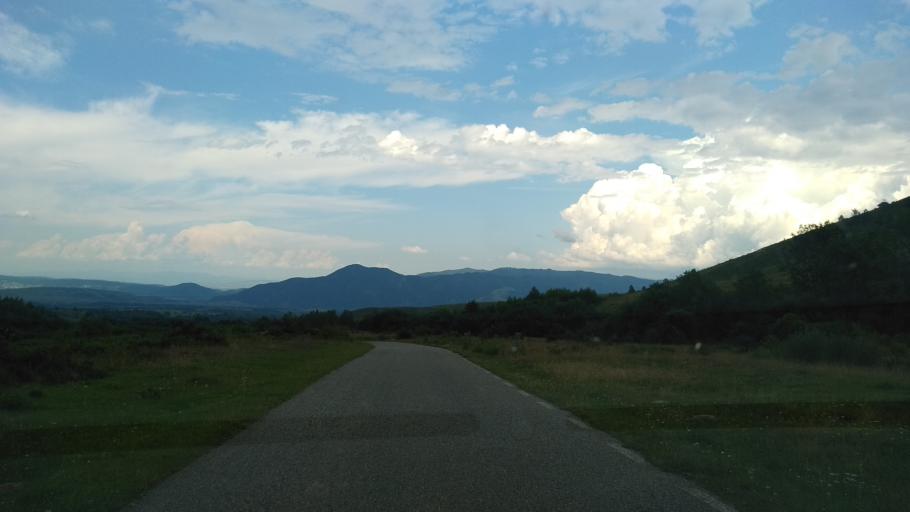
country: RO
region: Hunedoara
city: Salasu de Sus
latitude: 45.4775
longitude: 22.9627
